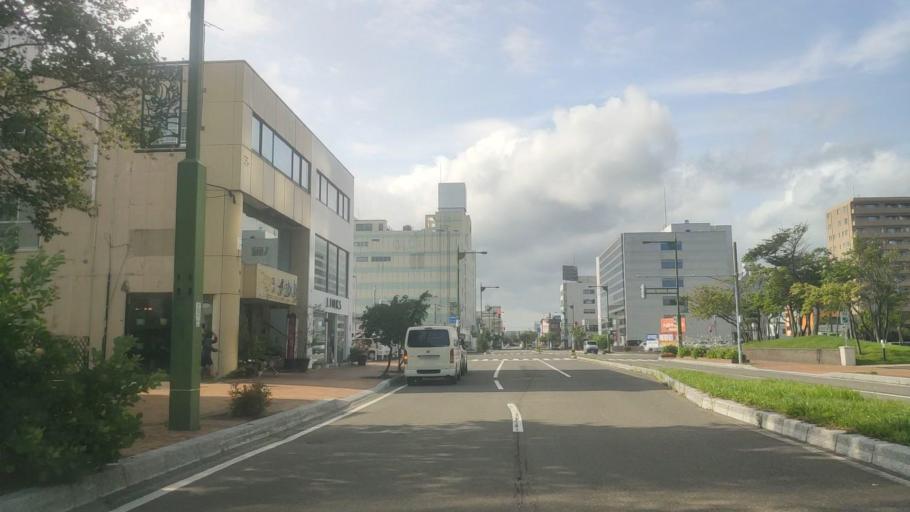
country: JP
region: Hokkaido
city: Tomakomai
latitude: 42.6368
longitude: 141.5992
